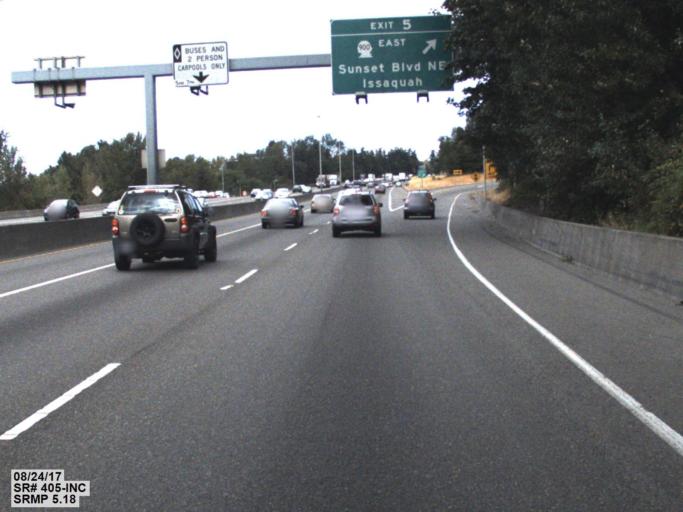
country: US
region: Washington
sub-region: King County
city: Renton
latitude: 47.4993
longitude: -122.1953
